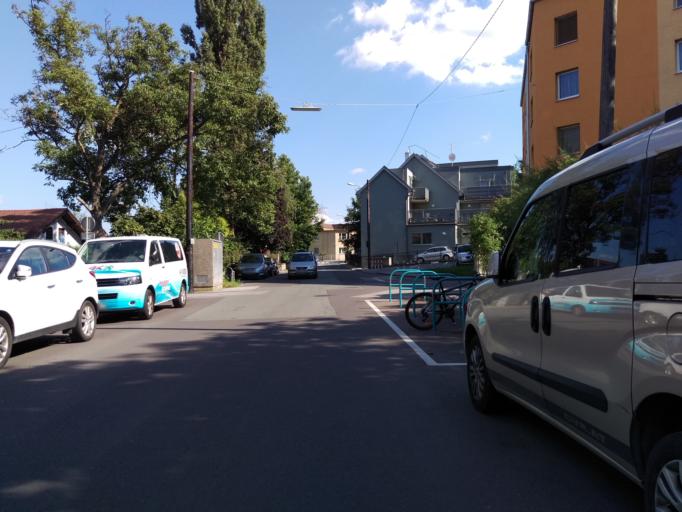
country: AT
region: Styria
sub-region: Graz Stadt
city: Wetzelsdorf
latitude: 47.0604
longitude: 15.3902
